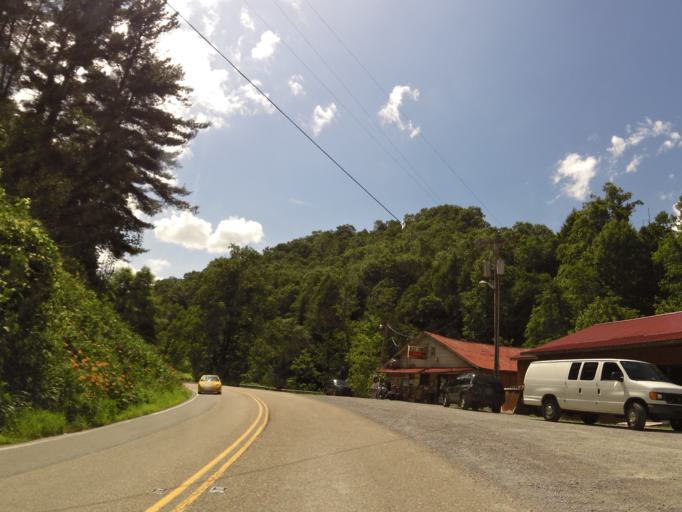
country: US
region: Virginia
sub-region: Lee County
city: Pennington Gap
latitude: 36.7682
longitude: -83.0994
